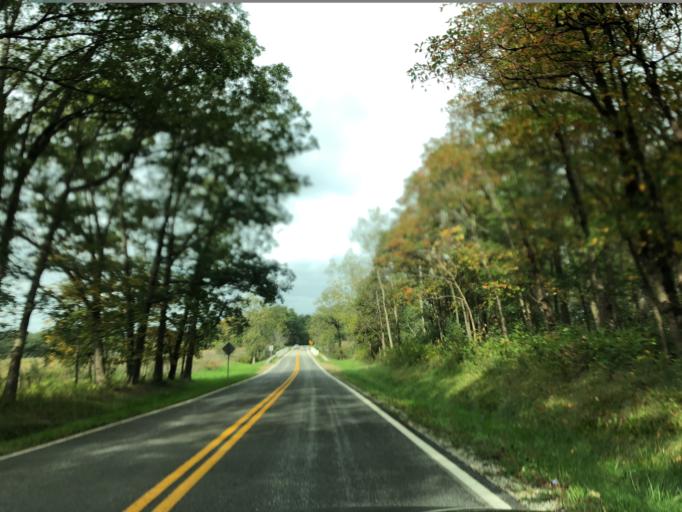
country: US
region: Ohio
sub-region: Summit County
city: Boston Heights
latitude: 41.2692
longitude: -81.5419
